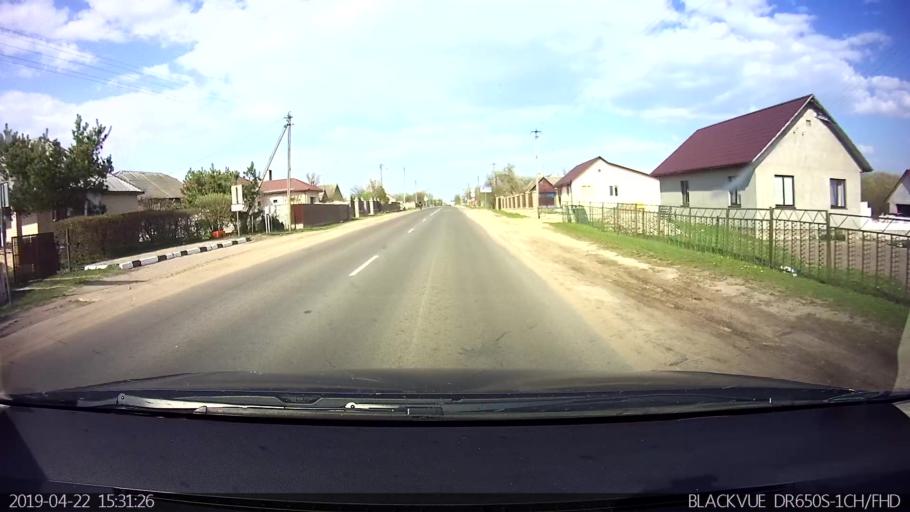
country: BY
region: Brest
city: Vysokaye
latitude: 52.4007
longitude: 23.3854
